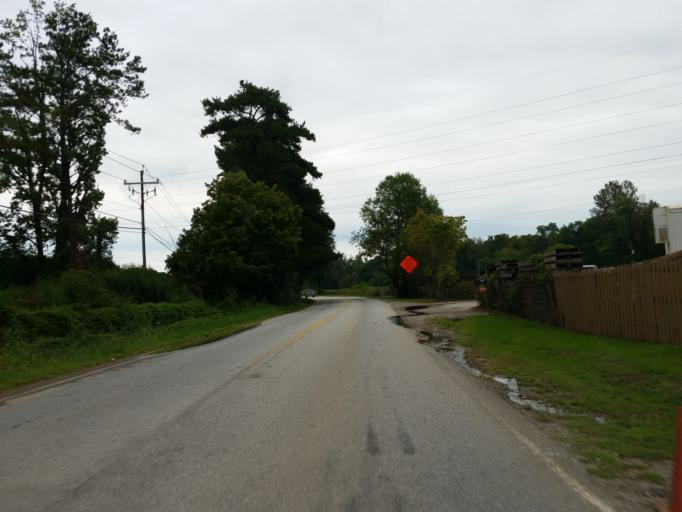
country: US
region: Georgia
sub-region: Cobb County
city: Vinings
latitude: 33.7990
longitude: -84.5060
